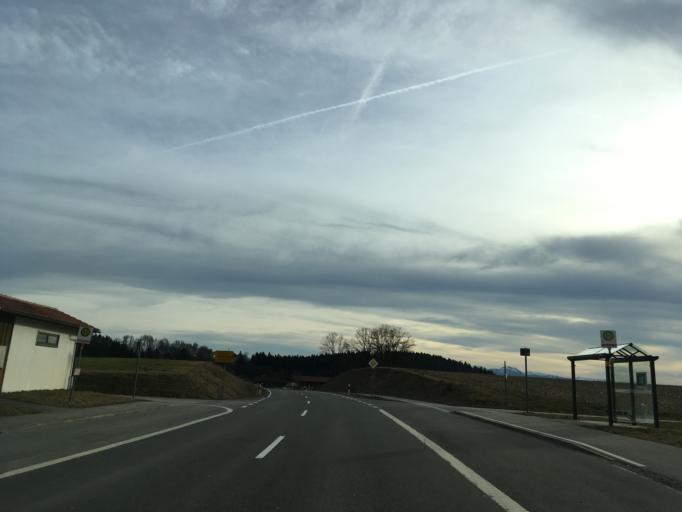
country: DE
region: Bavaria
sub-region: Upper Bavaria
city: Sochtenau
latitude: 47.9177
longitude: 12.2163
